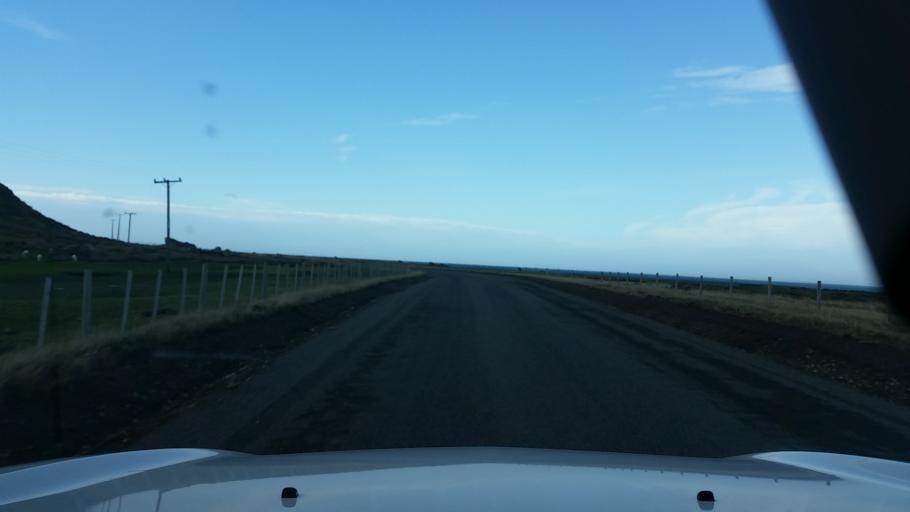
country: NZ
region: Wellington
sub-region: South Wairarapa District
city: Waipawa
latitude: -41.5999
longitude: 175.2364
